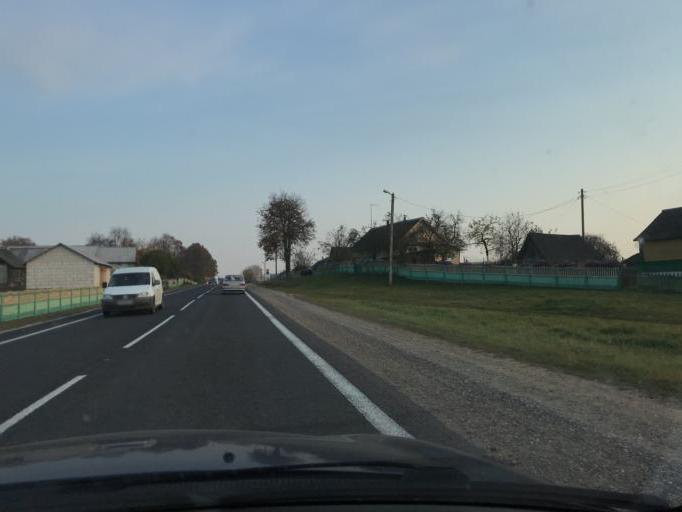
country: BY
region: Grodnenskaya
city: Karelichy
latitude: 53.5879
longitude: 26.1048
